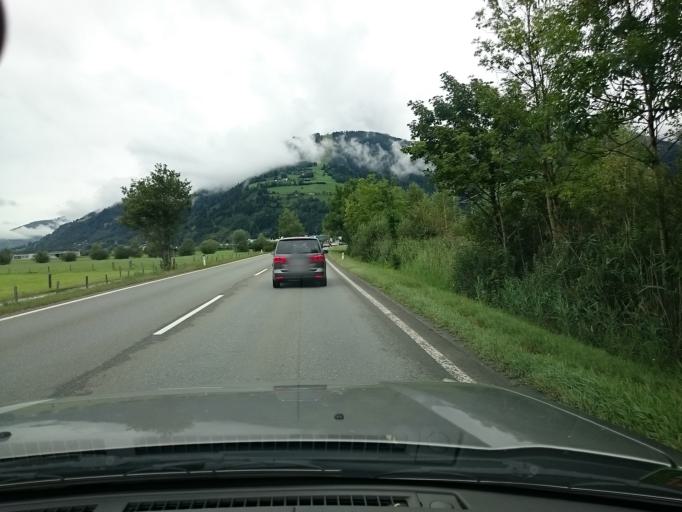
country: AT
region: Salzburg
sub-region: Politischer Bezirk Zell am See
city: Bruck an der Grossglocknerstrasse
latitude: 47.2921
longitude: 12.8014
